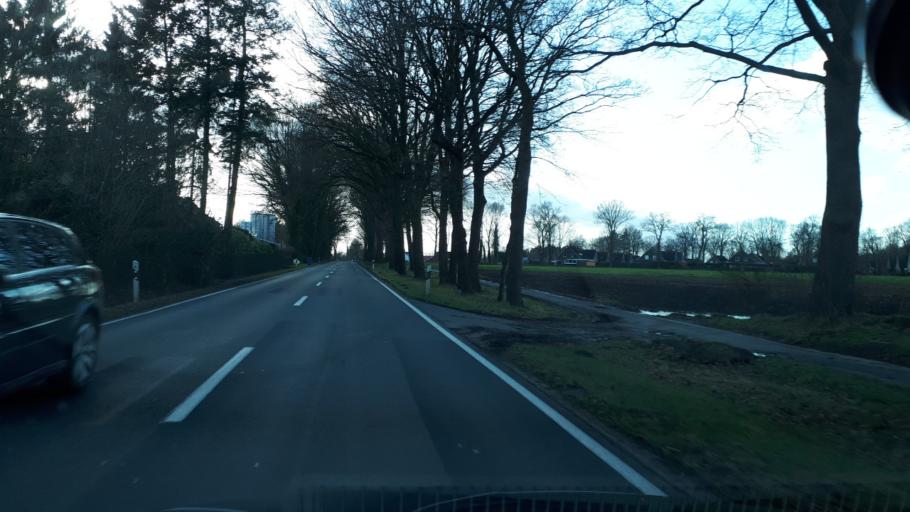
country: DE
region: Lower Saxony
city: Molbergen
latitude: 52.8561
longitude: 7.9396
